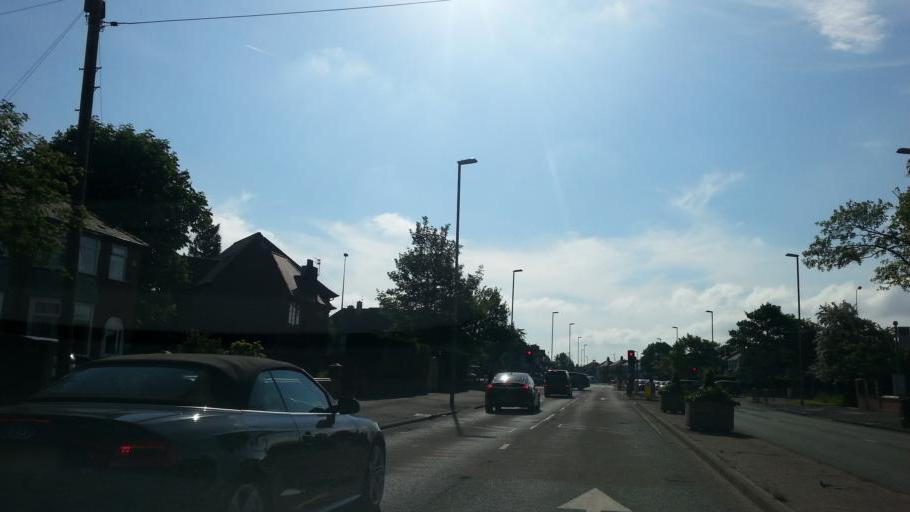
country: GB
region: England
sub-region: Manchester
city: Failsworth
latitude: 53.5227
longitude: -2.1663
